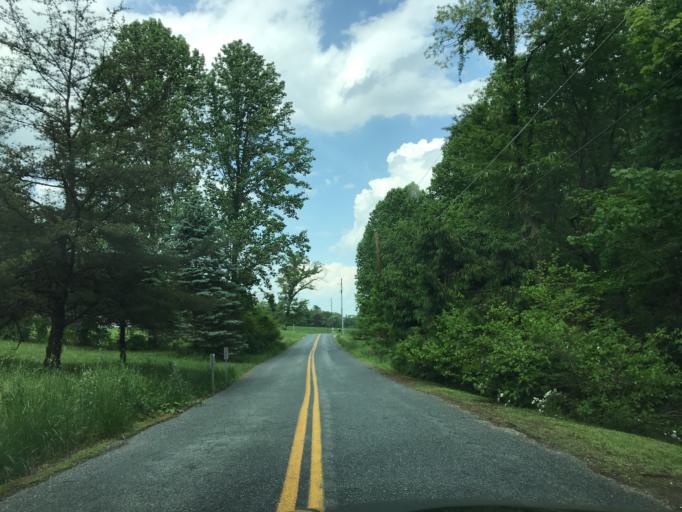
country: US
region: Pennsylvania
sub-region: York County
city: Susquehanna Trails
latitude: 39.7046
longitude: -76.3302
